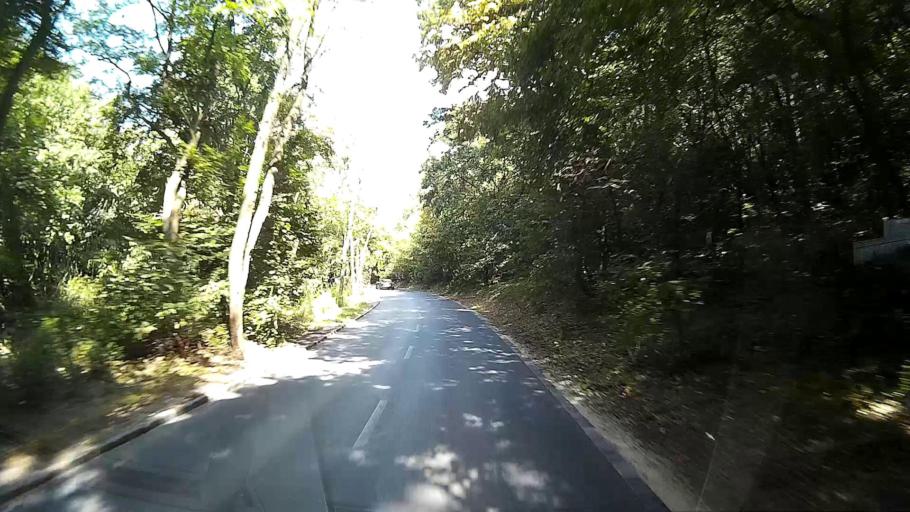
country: HU
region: Pest
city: Budakeszi
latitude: 47.5371
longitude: 18.9479
